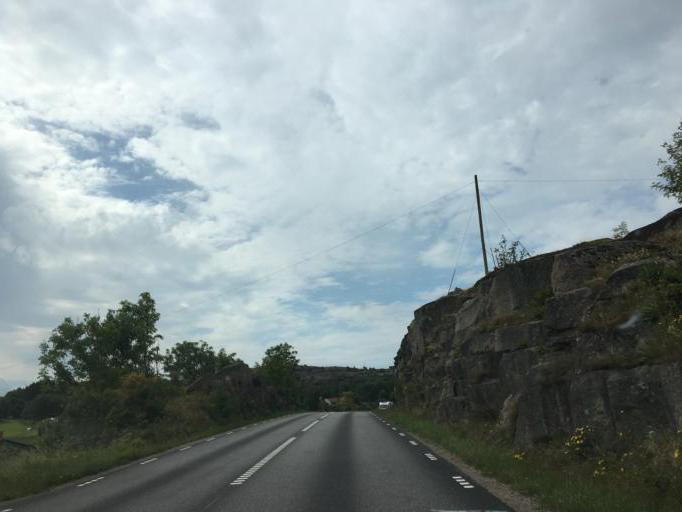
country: SE
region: Vaestra Goetaland
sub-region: Sotenas Kommun
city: Hunnebostrand
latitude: 58.4177
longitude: 11.2884
